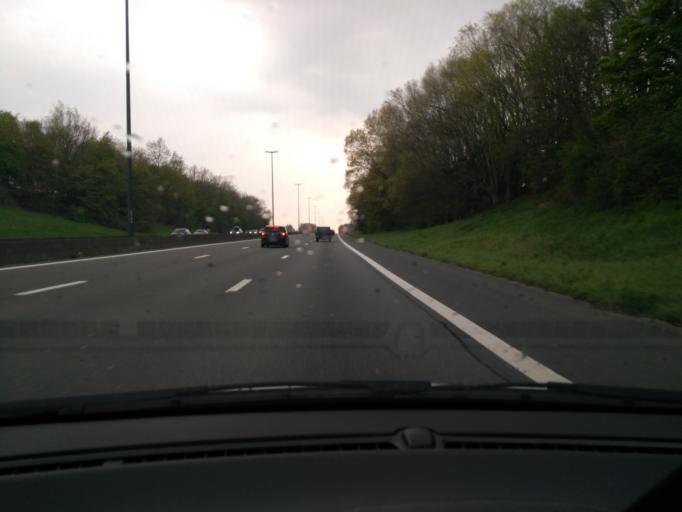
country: BE
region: Wallonia
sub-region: Province du Hainaut
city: Roeulx
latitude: 50.4810
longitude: 4.0482
